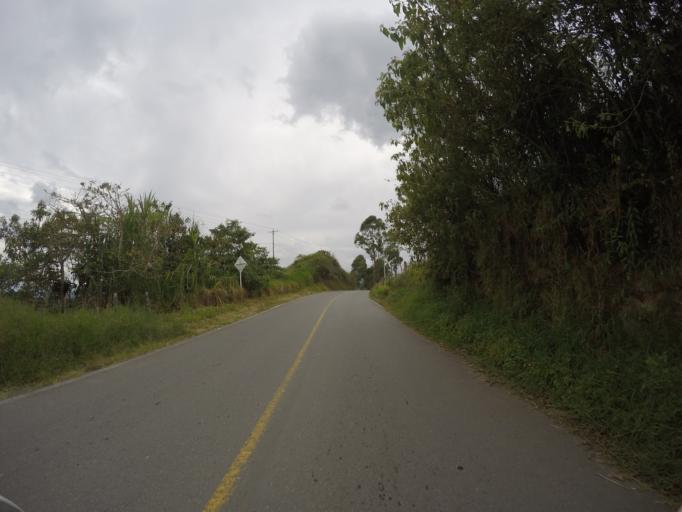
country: CO
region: Quindio
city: Filandia
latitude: 4.6611
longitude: -75.6726
